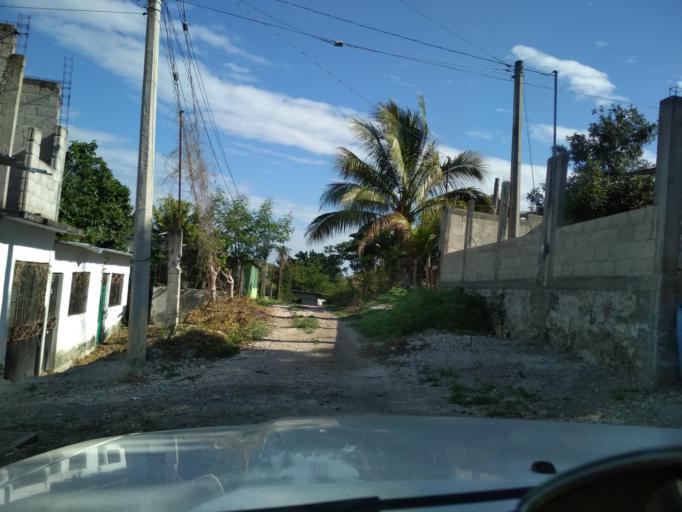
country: MX
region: Veracruz
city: Rinconada
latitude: 19.3560
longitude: -96.5607
